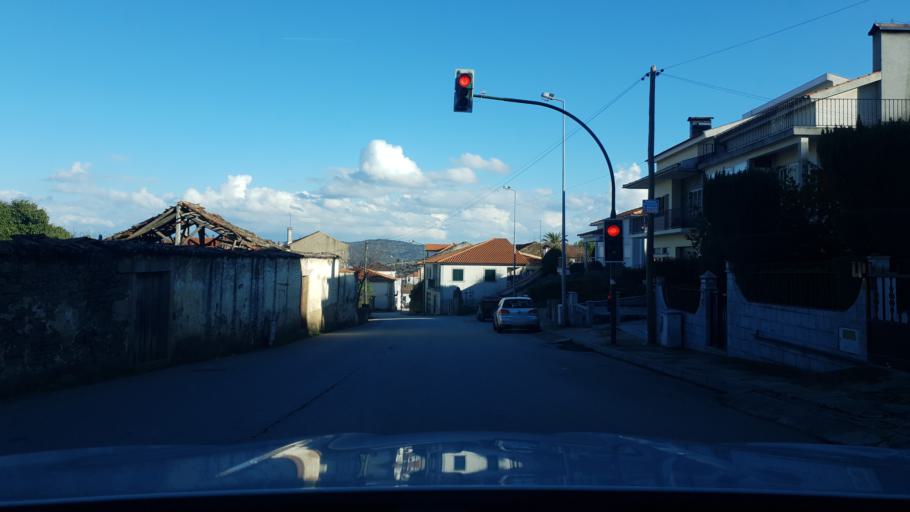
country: PT
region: Braganca
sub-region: Freixo de Espada A Cinta
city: Freixo de Espada a Cinta
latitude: 41.0935
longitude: -6.8114
